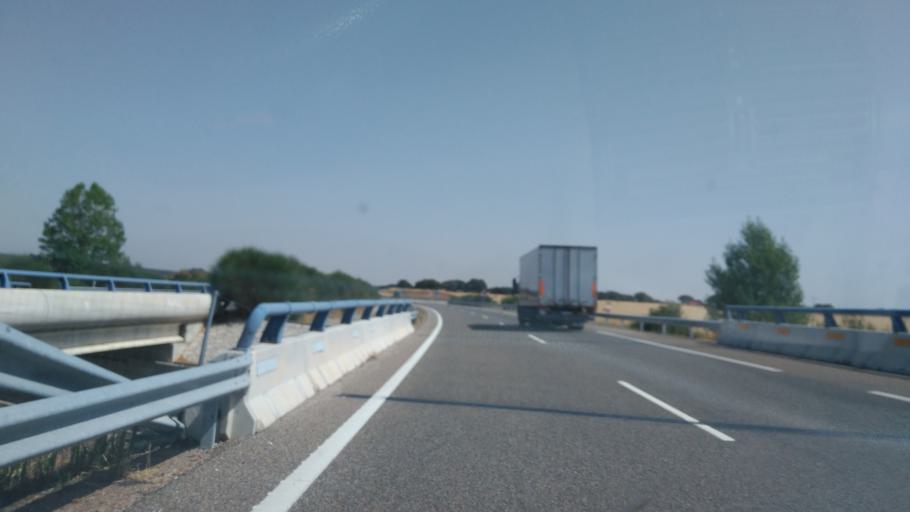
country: ES
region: Castille and Leon
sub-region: Provincia de Salamanca
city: Aldehuela de la Boveda
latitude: 40.8486
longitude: -6.0495
